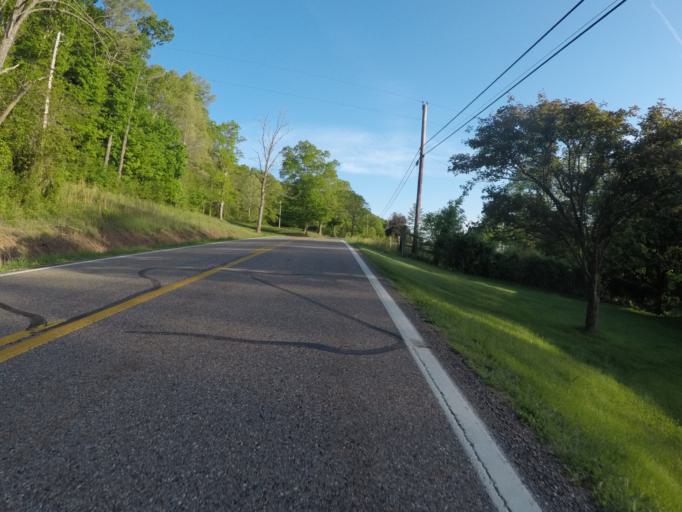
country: US
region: West Virginia
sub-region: Cabell County
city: Huntington
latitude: 38.5495
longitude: -82.4628
